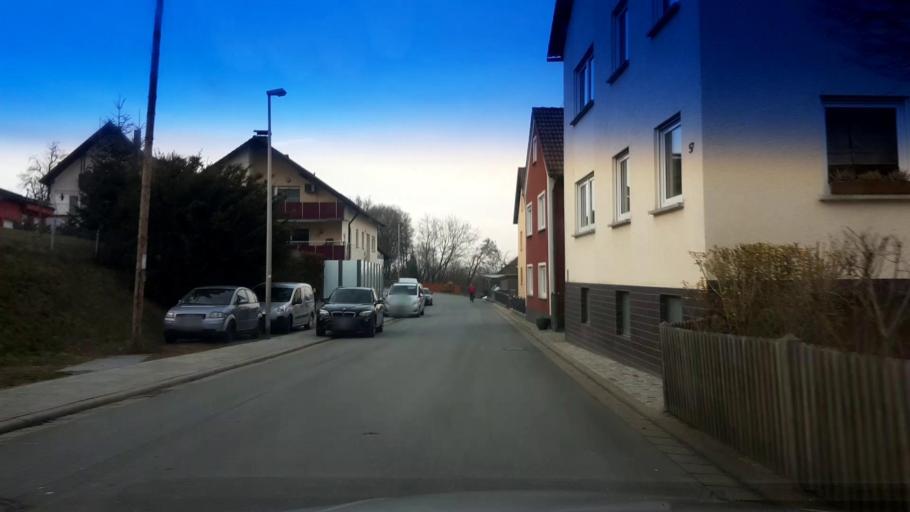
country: DE
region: Bavaria
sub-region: Upper Franconia
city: Altendorf
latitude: 49.7928
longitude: 10.9982
